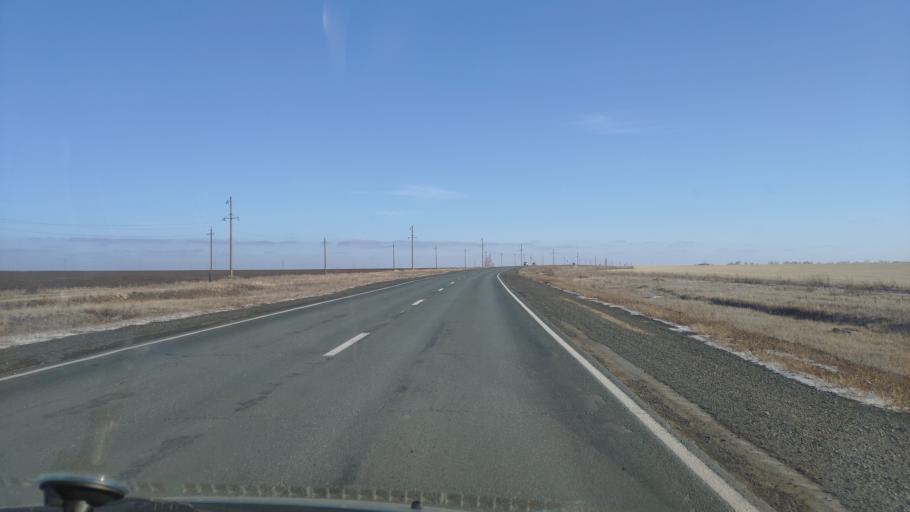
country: RU
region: Orenburg
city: Novorudnyy
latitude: 51.4353
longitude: 57.8955
